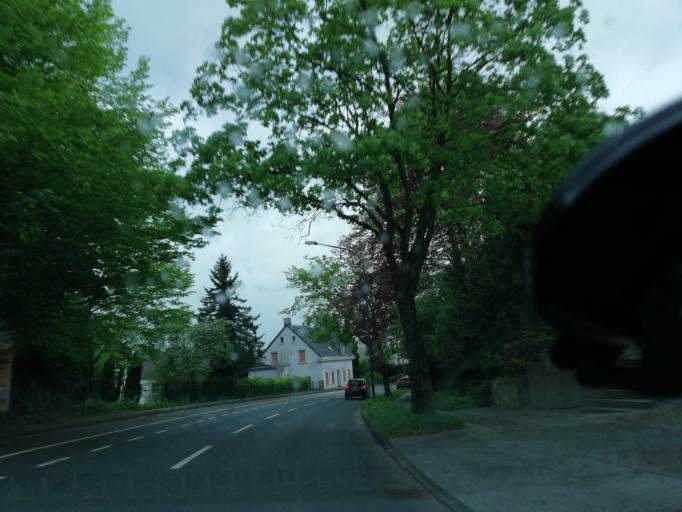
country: DE
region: North Rhine-Westphalia
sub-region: Regierungsbezirk Dusseldorf
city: Solingen
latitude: 51.2284
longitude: 7.0723
